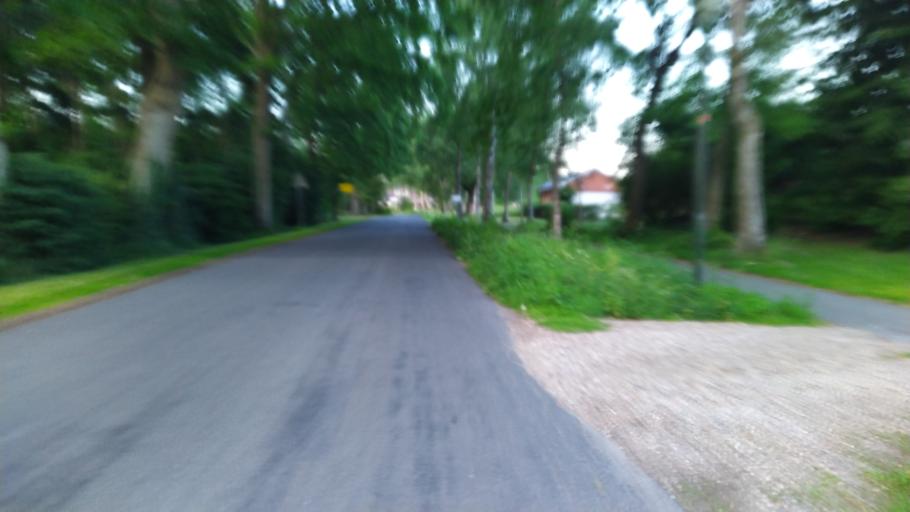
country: DE
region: Lower Saxony
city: Bremervorde
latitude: 53.4841
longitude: 9.1694
